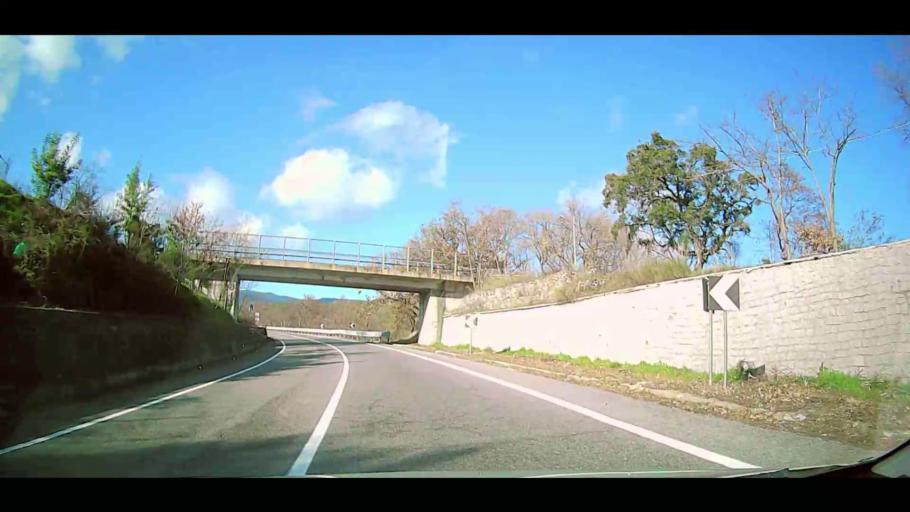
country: IT
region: Calabria
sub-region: Provincia di Crotone
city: Cerenzia
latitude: 39.2480
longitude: 16.7882
